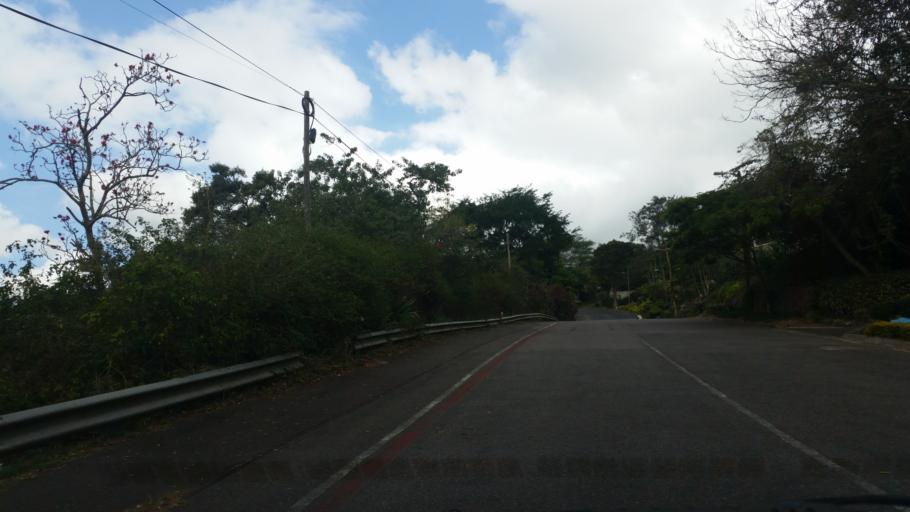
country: ZA
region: KwaZulu-Natal
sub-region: eThekwini Metropolitan Municipality
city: Berea
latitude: -29.8249
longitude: 30.9259
